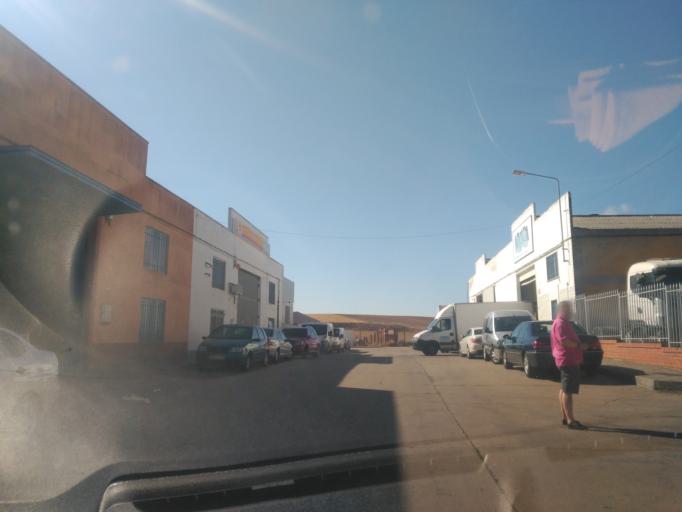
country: ES
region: Castille and Leon
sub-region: Provincia de Salamanca
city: Villares de la Reina
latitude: 40.9905
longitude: -5.6377
